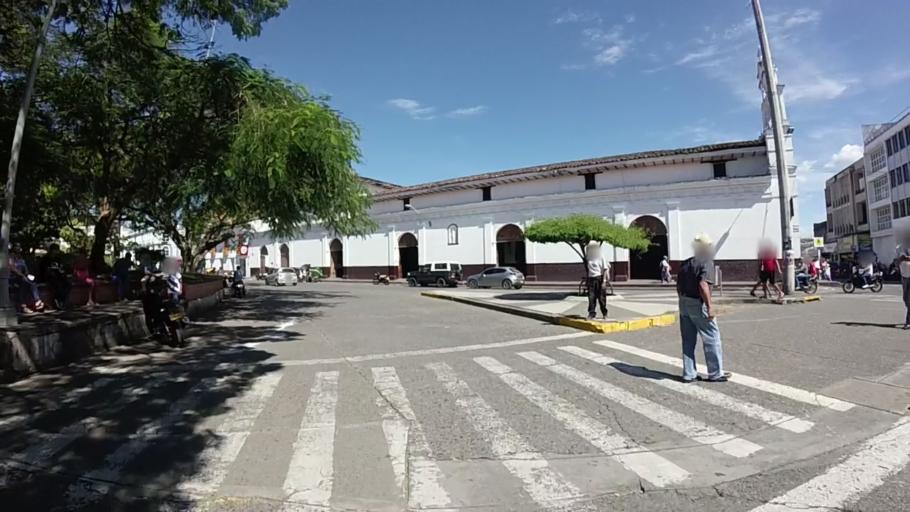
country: CO
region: Valle del Cauca
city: Cartago
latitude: 4.7493
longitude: -75.9135
